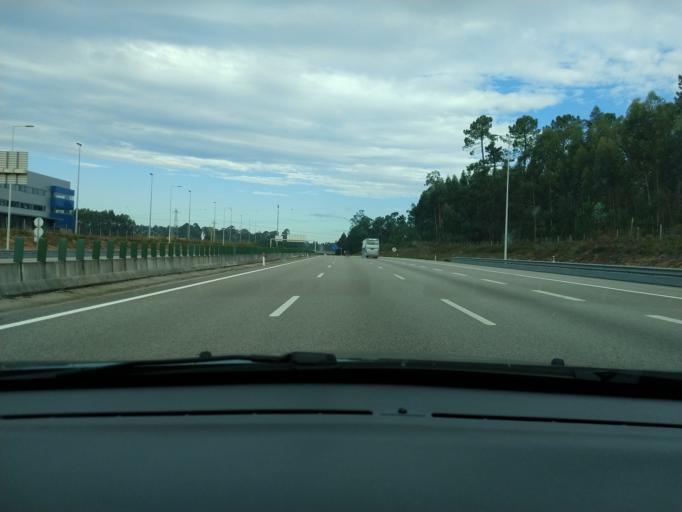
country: PT
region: Aveiro
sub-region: Estarreja
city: Beduido
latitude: 40.7831
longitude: -8.5450
